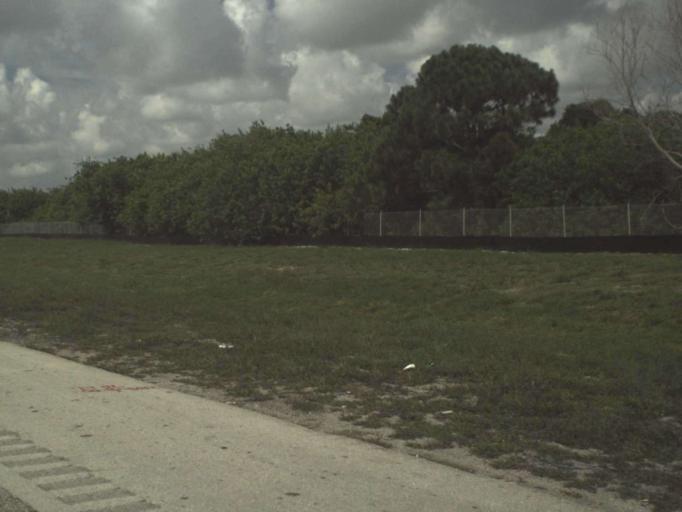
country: US
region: Florida
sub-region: Palm Beach County
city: Highland Beach
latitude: 26.3997
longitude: -80.0905
